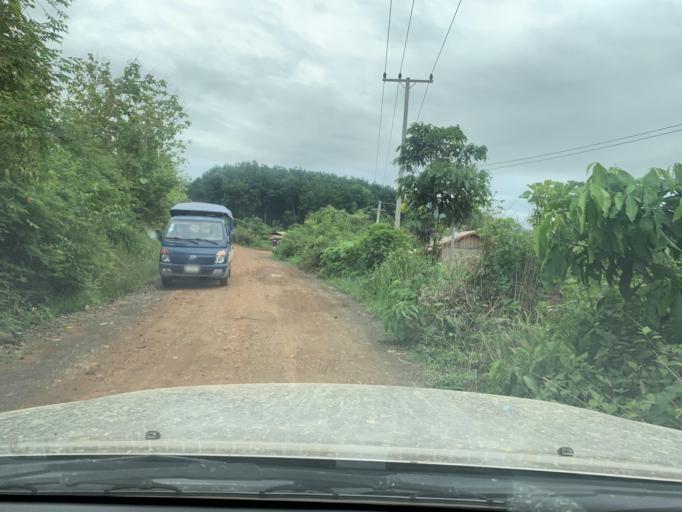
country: TH
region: Nan
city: Mae Charim
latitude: 18.4123
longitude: 101.4411
